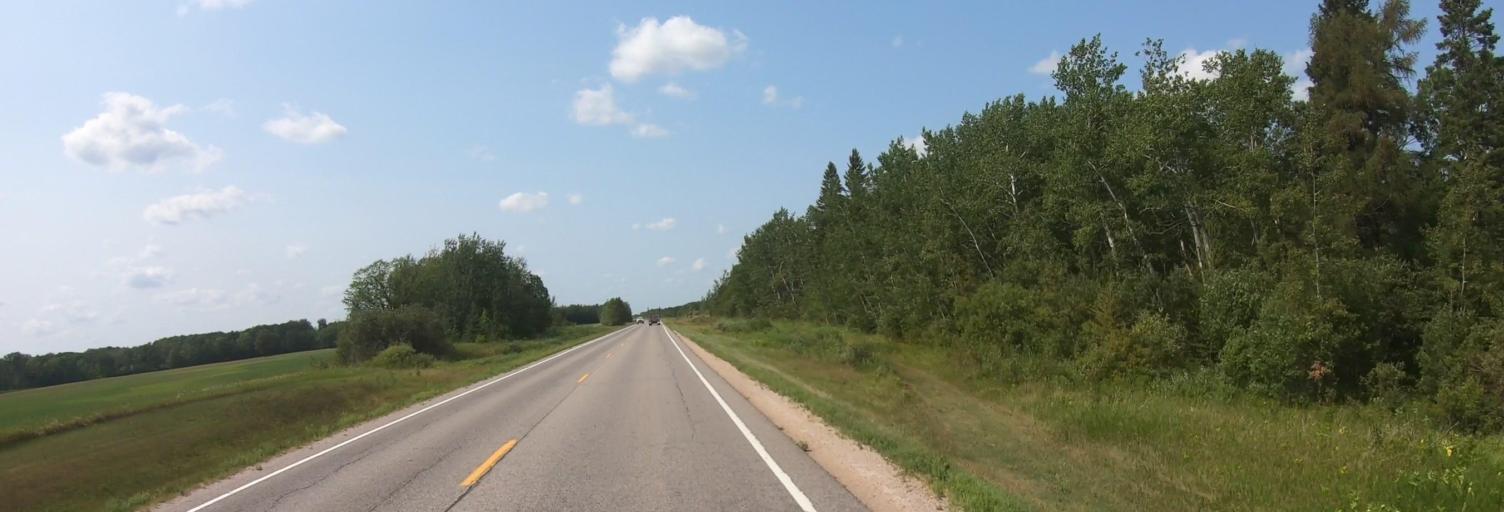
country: US
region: Minnesota
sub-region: Roseau County
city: Warroad
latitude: 48.8048
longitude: -95.1041
